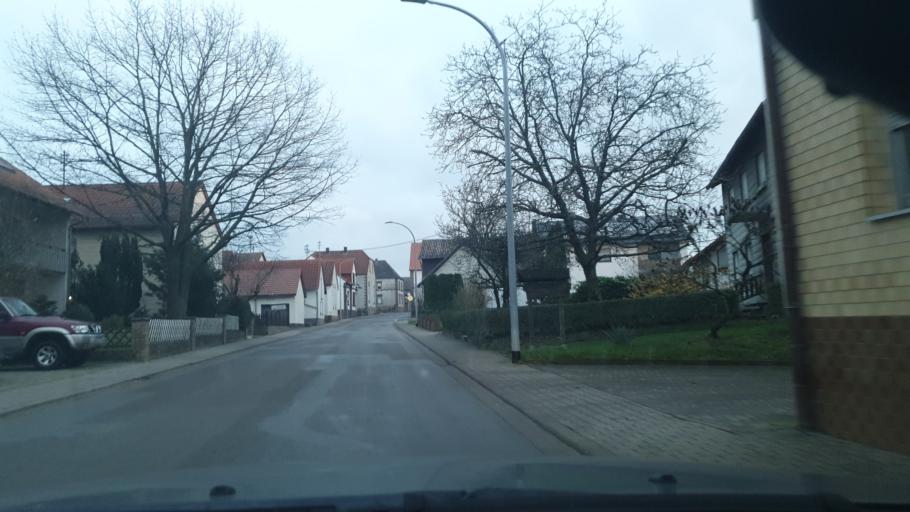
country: DE
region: Rheinland-Pfalz
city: Martinshohe
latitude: 49.3649
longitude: 7.4739
